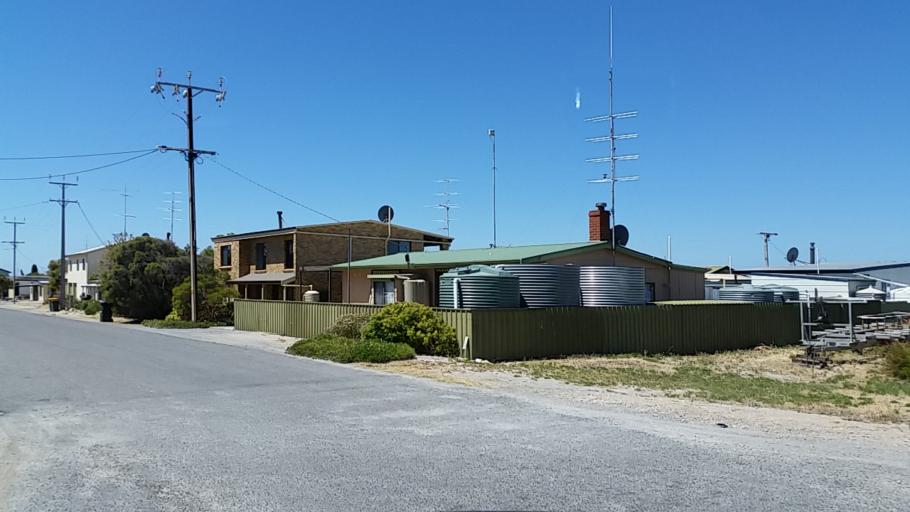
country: AU
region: South Australia
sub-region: Yorke Peninsula
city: Honiton
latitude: -35.2426
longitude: 136.9787
